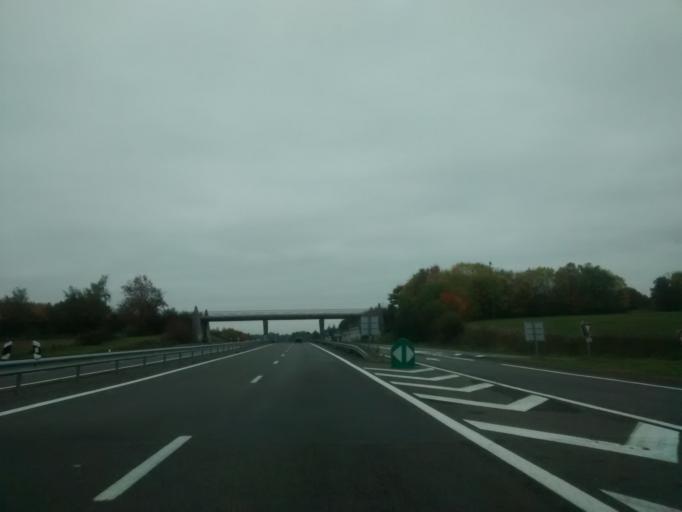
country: FR
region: Brittany
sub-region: Departement d'Ille-et-Vilaine
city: Saint-Pierre-de-Plesguen
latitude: 48.4583
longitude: -1.9178
